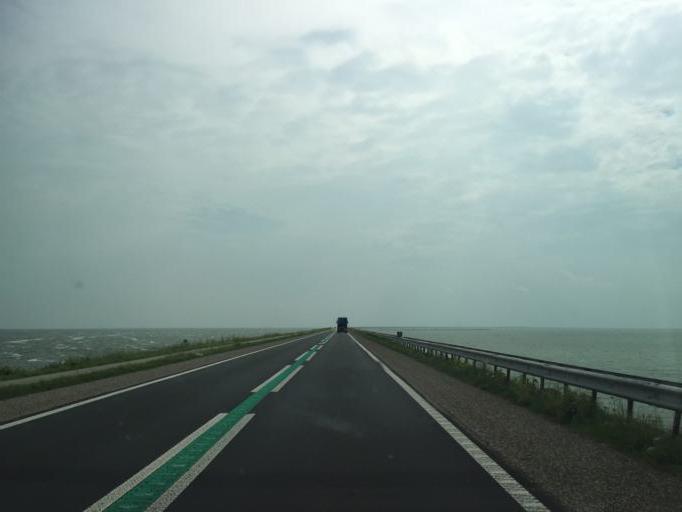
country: NL
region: North Holland
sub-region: Gemeente Enkhuizen
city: Enkhuizen
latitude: 52.6880
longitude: 5.3143
